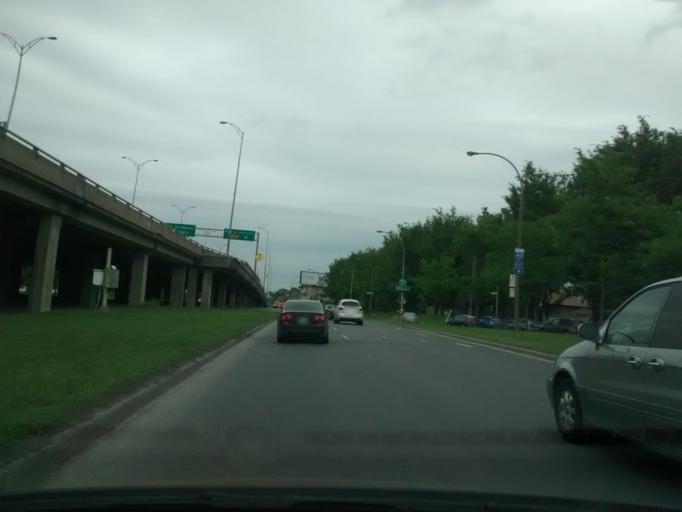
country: CA
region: Quebec
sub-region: Montreal
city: Saint-Leonard
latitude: 45.5566
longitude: -73.6159
